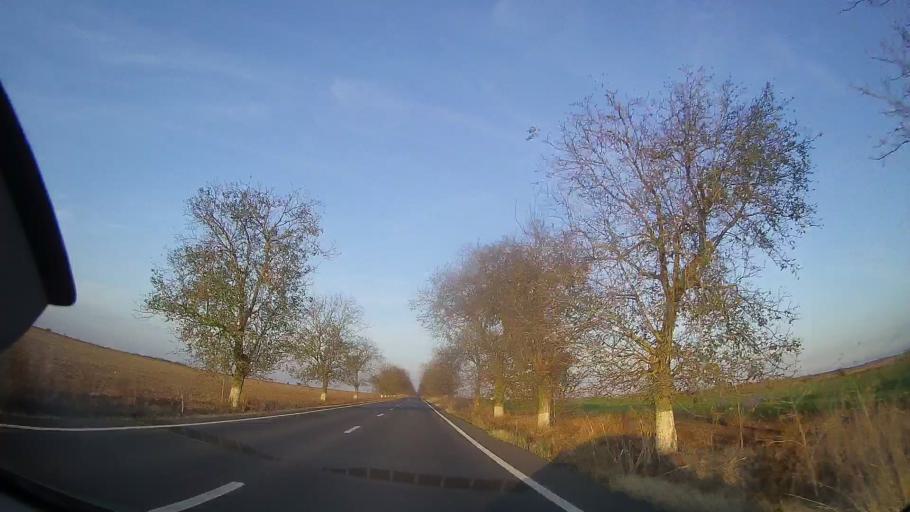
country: RO
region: Constanta
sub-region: Comuna Amzacea
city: Amzacea
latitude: 43.9474
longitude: 28.3785
